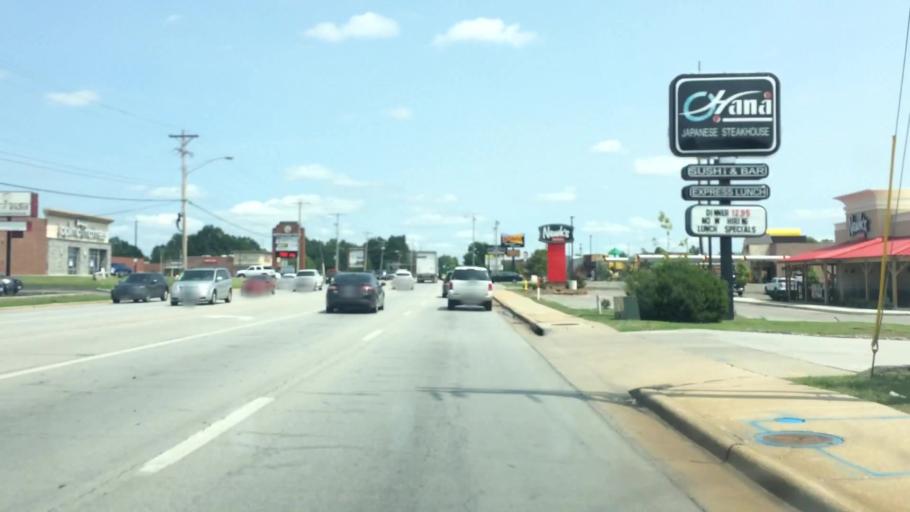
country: US
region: Missouri
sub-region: Greene County
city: Springfield
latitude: 37.1598
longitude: -93.2942
